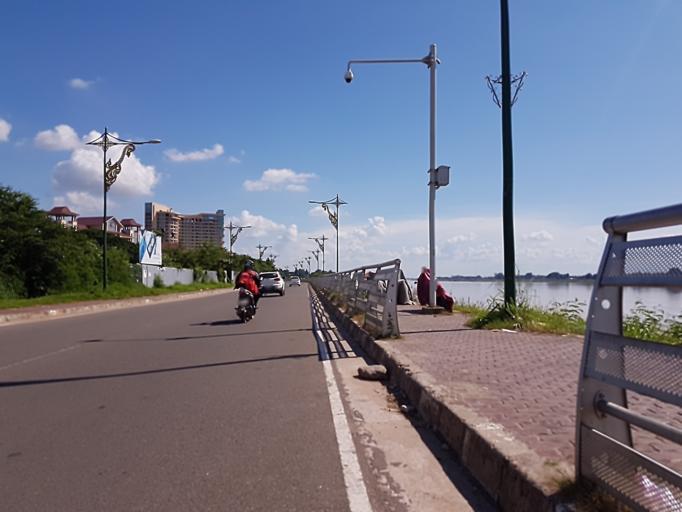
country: LA
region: Vientiane
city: Vientiane
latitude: 17.9474
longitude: 102.6157
